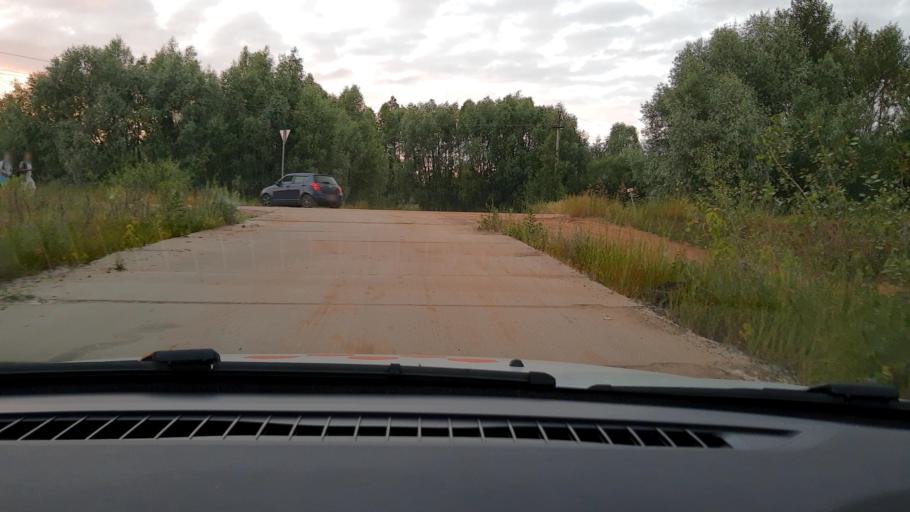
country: RU
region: Nizjnij Novgorod
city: Neklyudovo
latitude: 56.3644
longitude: 43.9391
